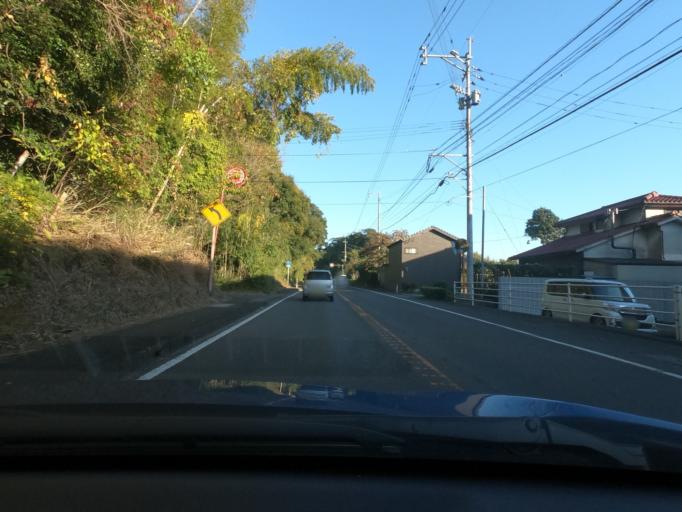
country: JP
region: Kagoshima
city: Satsumasendai
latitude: 31.8473
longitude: 130.2528
